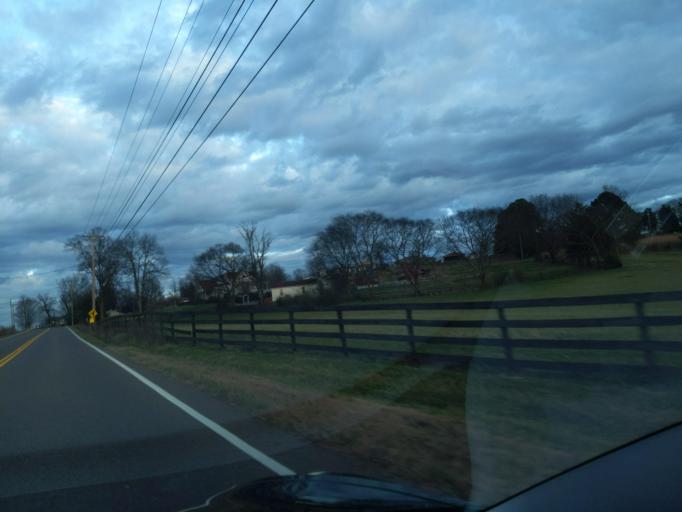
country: US
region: Tennessee
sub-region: Jefferson County
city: Dandridge
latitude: 35.9993
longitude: -83.4429
